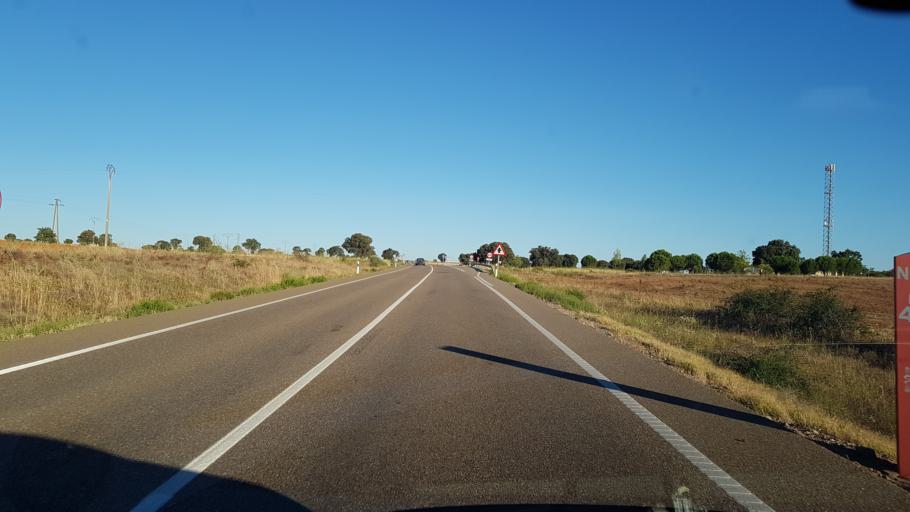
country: ES
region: Castille and Leon
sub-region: Provincia de Zamora
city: Palacios del Pan
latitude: 41.5411
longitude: -5.8608
